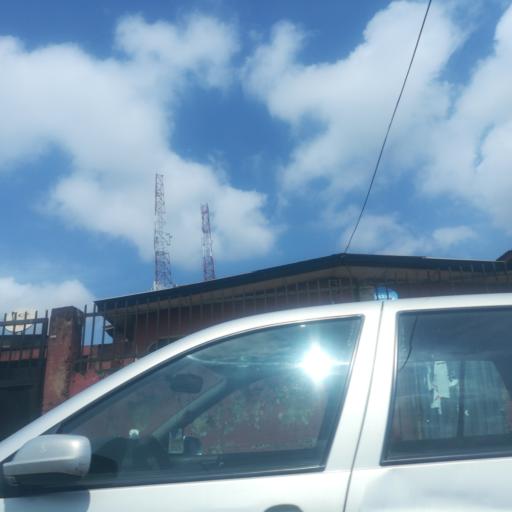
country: NG
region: Lagos
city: Ojota
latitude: 6.5951
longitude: 3.3867
